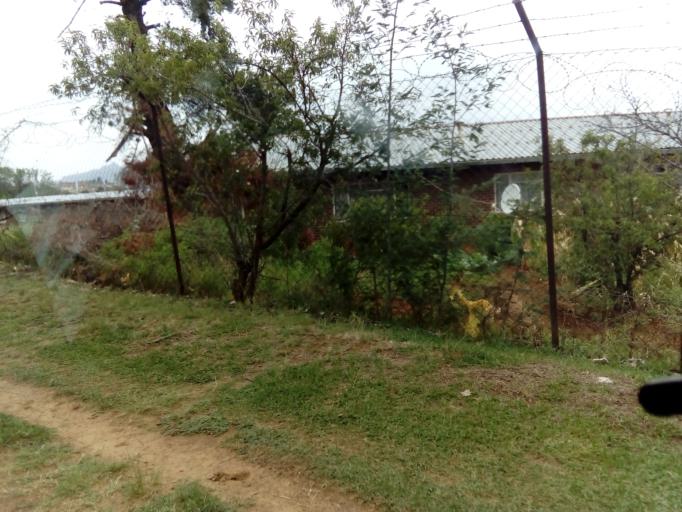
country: LS
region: Berea
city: Teyateyaneng
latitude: -29.1058
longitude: 27.9587
